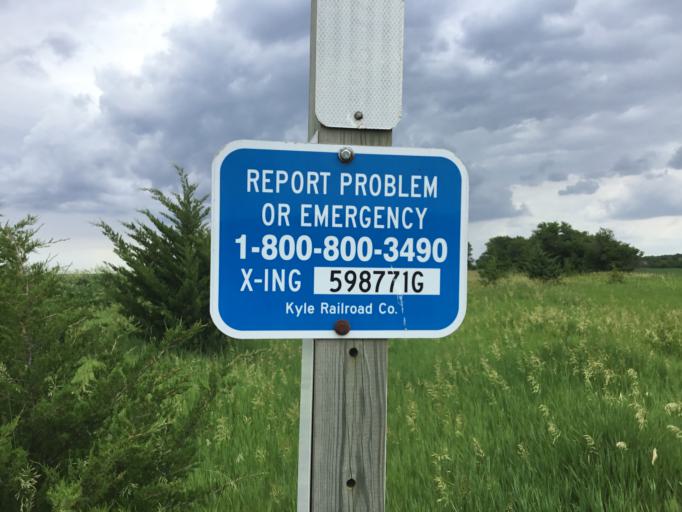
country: US
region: Kansas
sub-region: Republic County
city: Belleville
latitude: 39.8705
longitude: -97.5766
